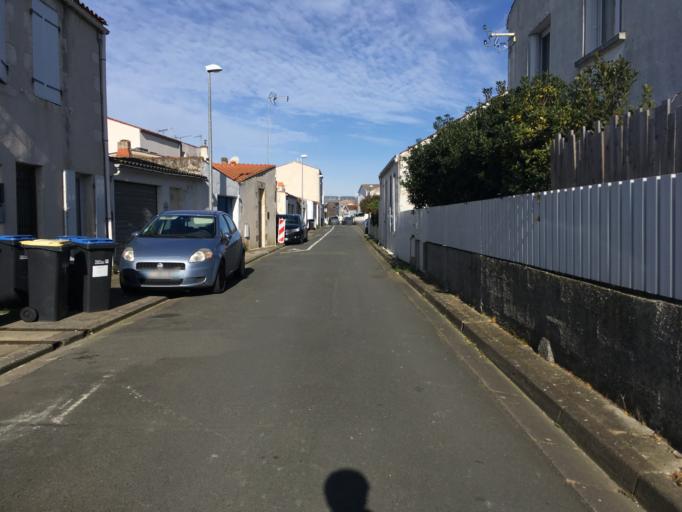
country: FR
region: Poitou-Charentes
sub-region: Departement de la Charente-Maritime
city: La Rochelle
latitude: 46.1477
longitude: -1.1427
